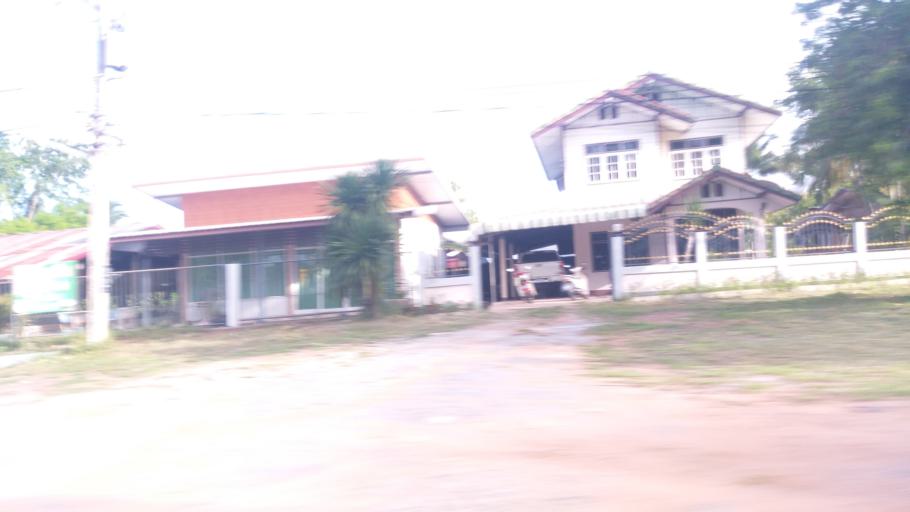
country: TH
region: Chaiyaphum
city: Ban Thaen
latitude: 16.3940
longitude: 102.3317
